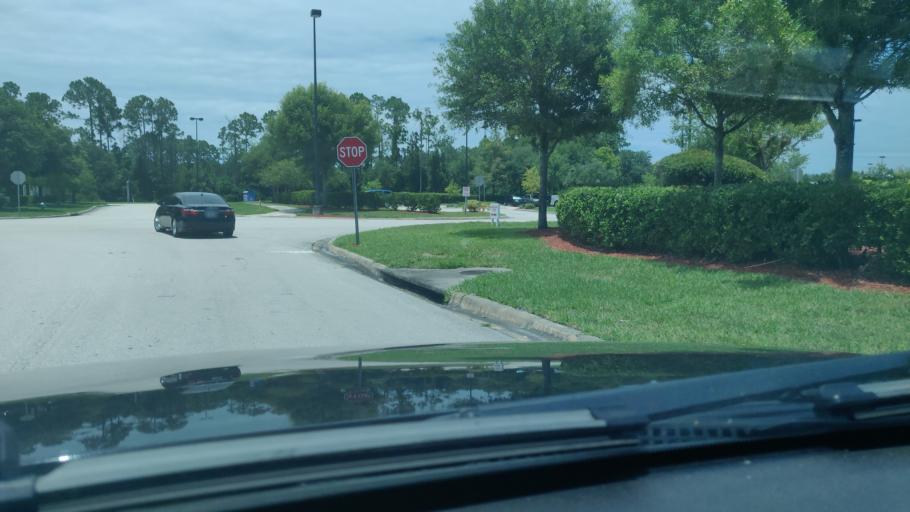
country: US
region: Florida
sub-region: Flagler County
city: Palm Coast
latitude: 29.5550
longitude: -81.2250
